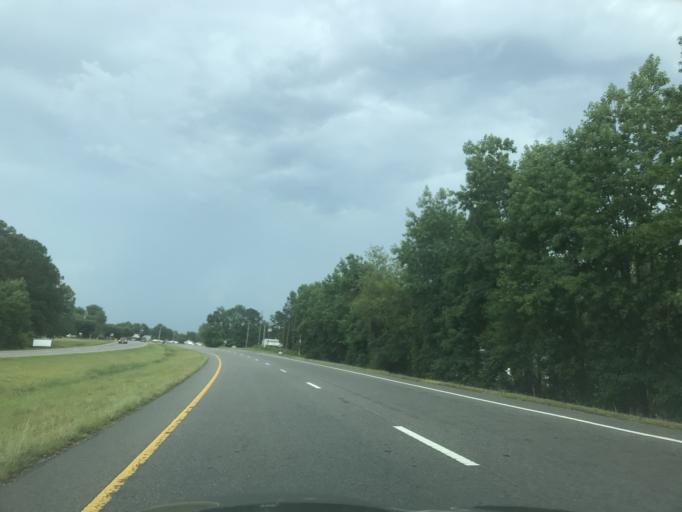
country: US
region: North Carolina
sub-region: Johnston County
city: Wilsons Mills
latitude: 35.5887
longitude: -78.4072
